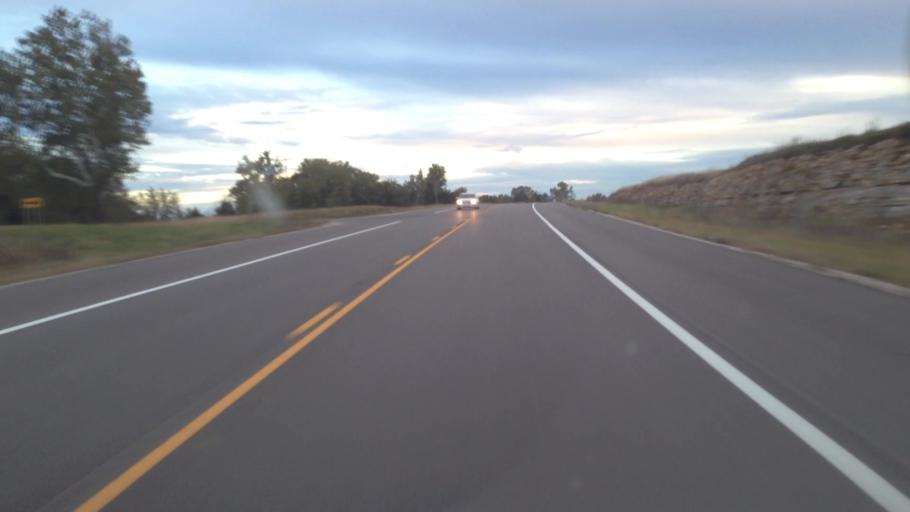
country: US
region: Kansas
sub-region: Anderson County
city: Garnett
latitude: 38.3317
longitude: -95.2489
